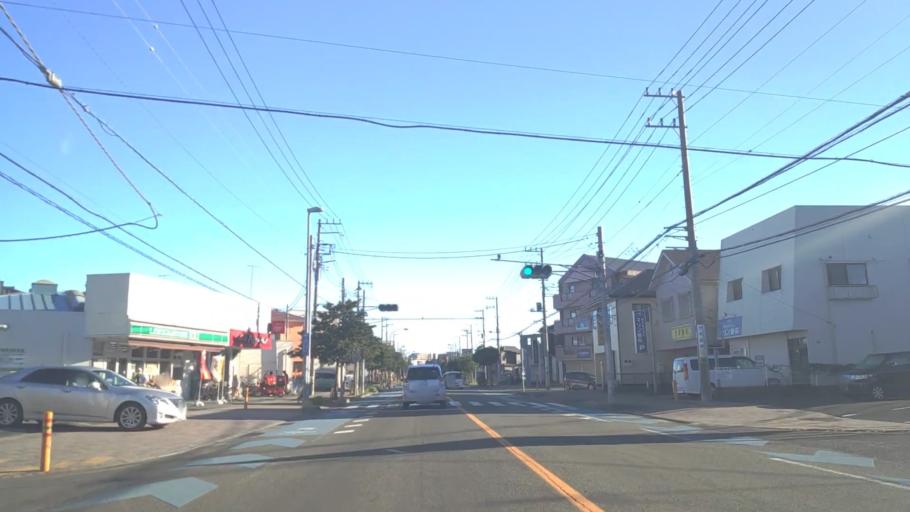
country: JP
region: Kanagawa
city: Chigasaki
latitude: 35.3469
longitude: 139.3975
